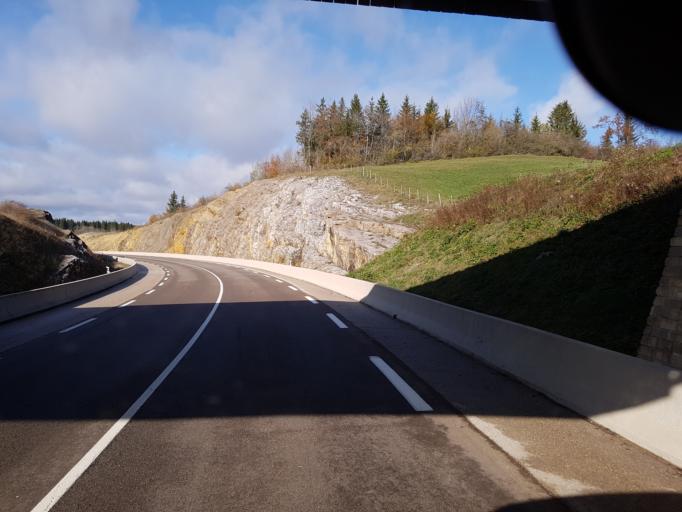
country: FR
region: Franche-Comte
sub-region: Departement du Jura
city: Morbier
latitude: 46.5824
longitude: 5.9584
